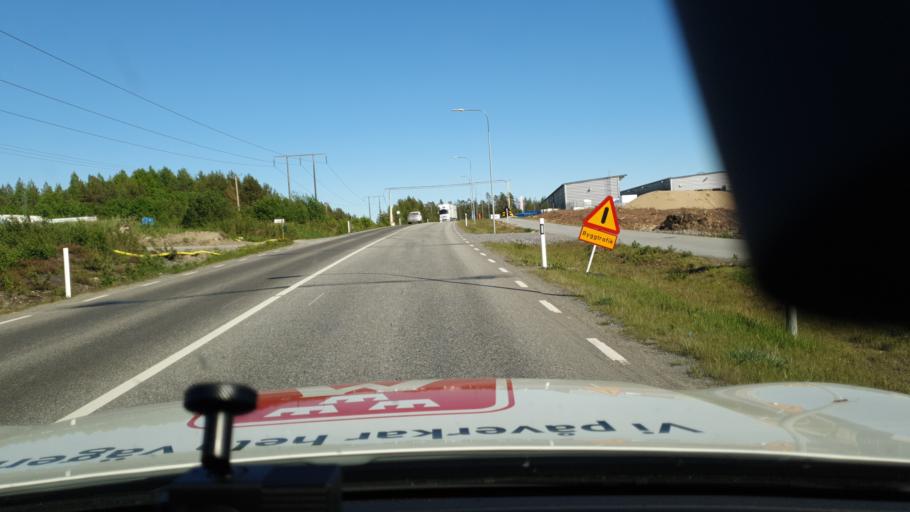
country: SE
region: Vaesterbotten
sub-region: Umea Kommun
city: Roback
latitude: 63.8490
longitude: 20.1503
